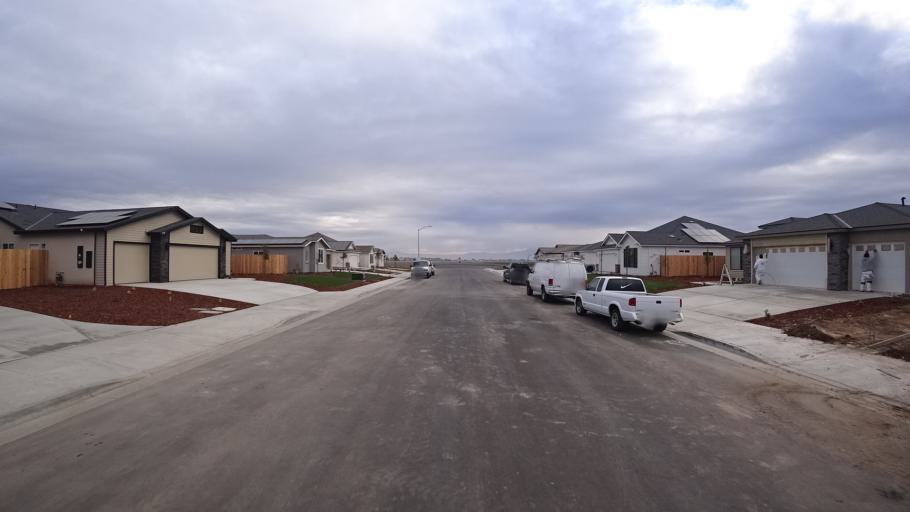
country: US
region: California
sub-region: Kern County
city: Greenfield
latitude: 35.2941
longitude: -119.0888
